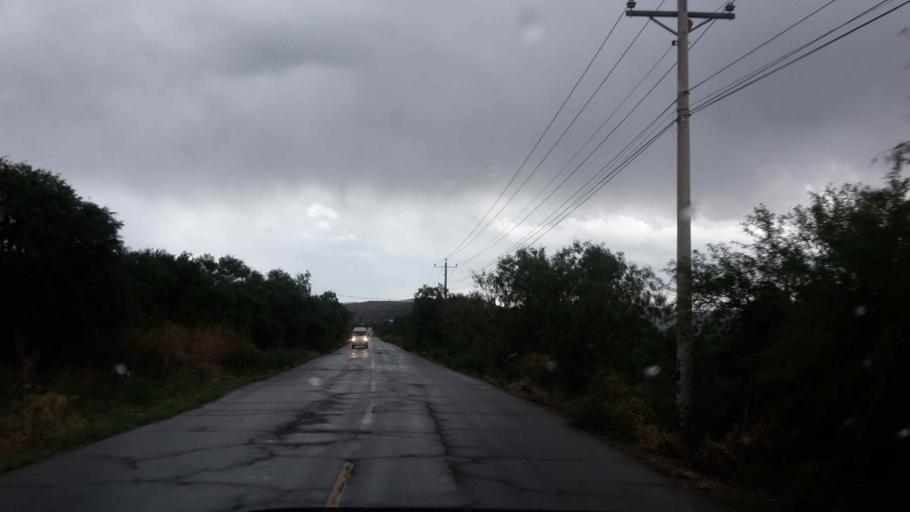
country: BO
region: Cochabamba
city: Tarata
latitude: -17.5727
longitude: -66.0658
